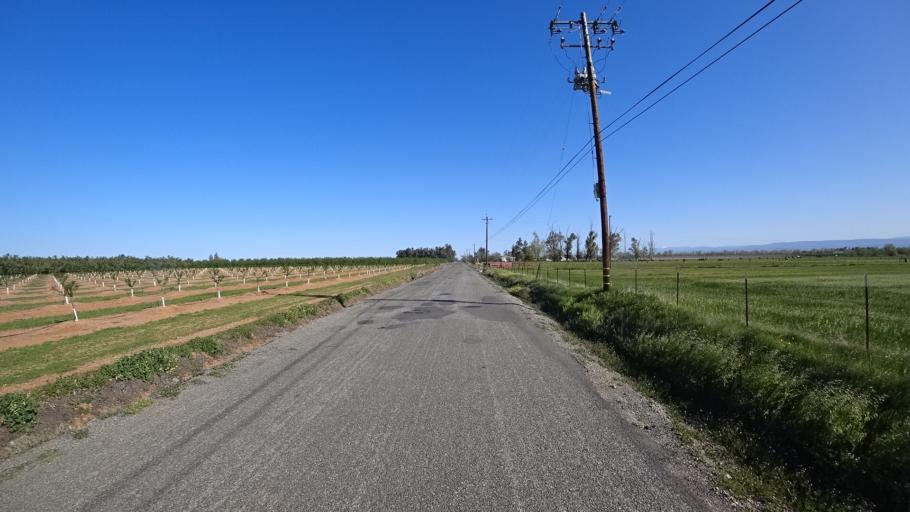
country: US
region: California
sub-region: Glenn County
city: Hamilton City
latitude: 39.7777
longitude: -122.0666
